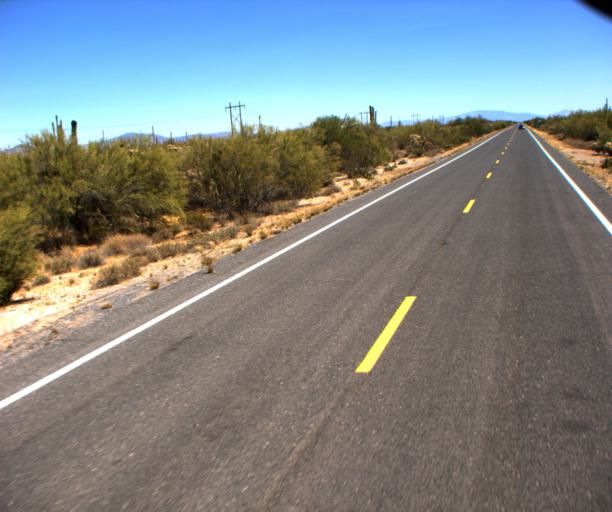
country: US
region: Arizona
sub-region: Pinal County
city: Florence
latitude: 32.8393
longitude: -111.2201
